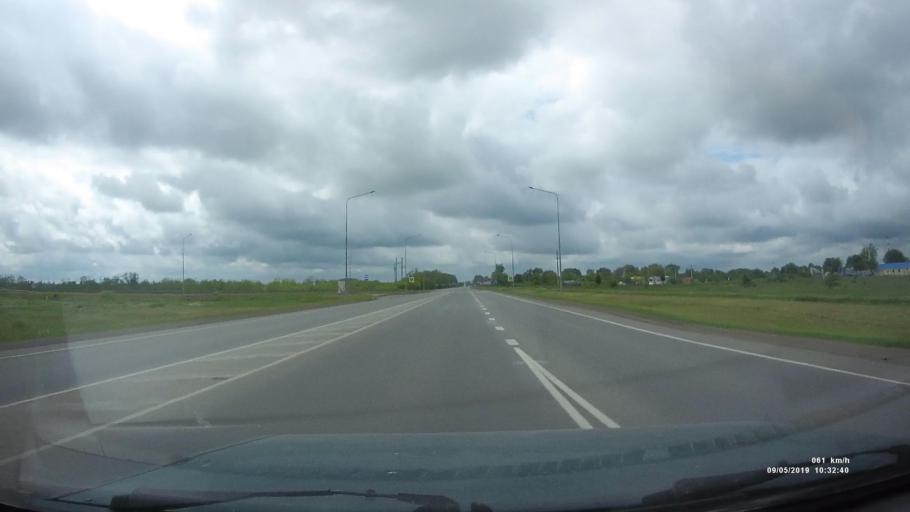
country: RU
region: Rostov
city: Azov
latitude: 47.0703
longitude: 39.4259
